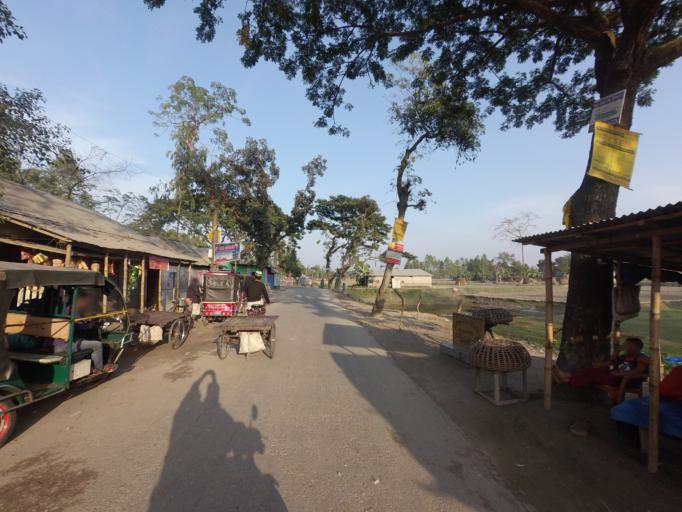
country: BD
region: Rajshahi
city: Saidpur
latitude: 25.9953
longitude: 88.7469
